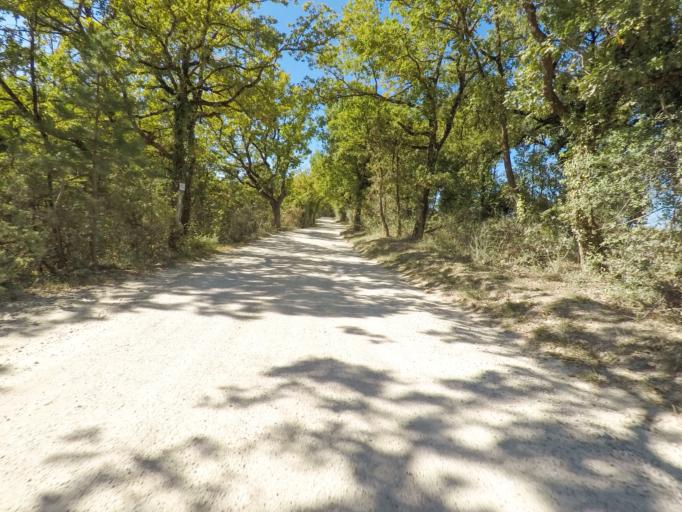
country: IT
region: Tuscany
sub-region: Provincia di Siena
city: Castellina in Chianti
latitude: 43.4402
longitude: 11.3092
